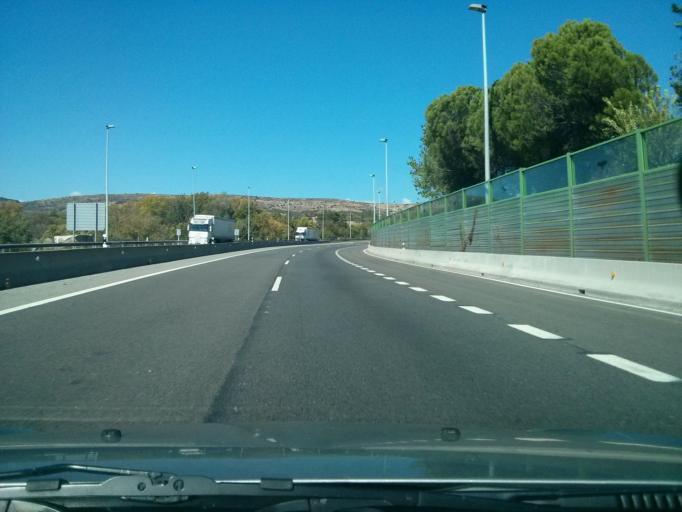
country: ES
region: Madrid
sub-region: Provincia de Madrid
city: La Cabrera
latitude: 40.9235
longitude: -3.6172
